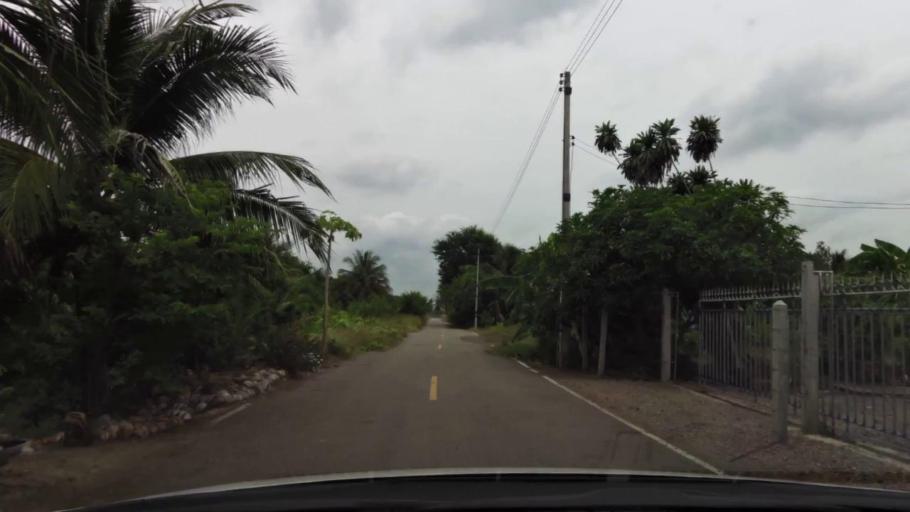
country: TH
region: Samut Sakhon
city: Ban Phaeo
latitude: 13.6111
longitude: 100.0325
